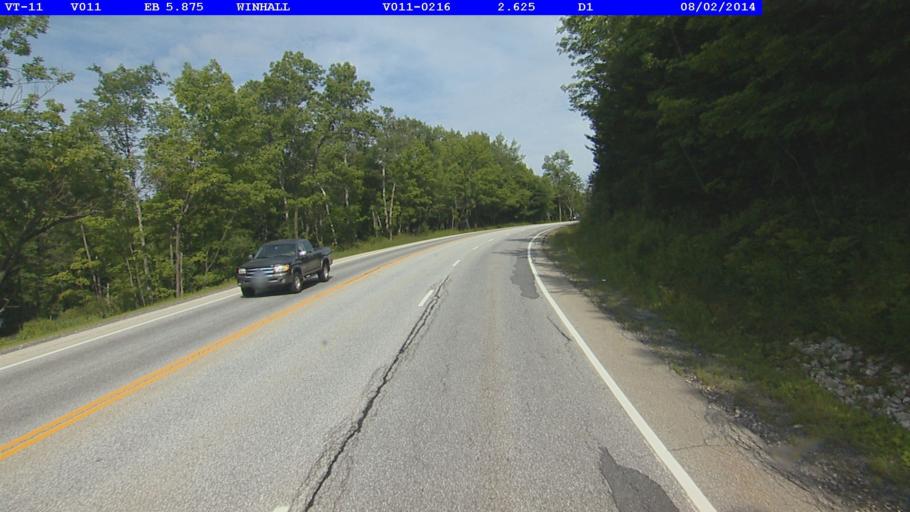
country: US
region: Vermont
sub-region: Bennington County
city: Manchester Center
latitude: 43.2068
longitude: -72.9704
